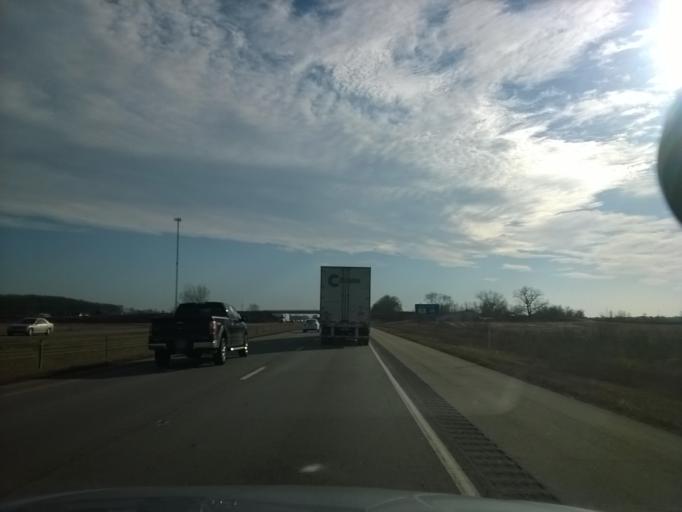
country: US
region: Indiana
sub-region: Johnson County
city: Edinburgh
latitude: 39.3800
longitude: -85.9429
